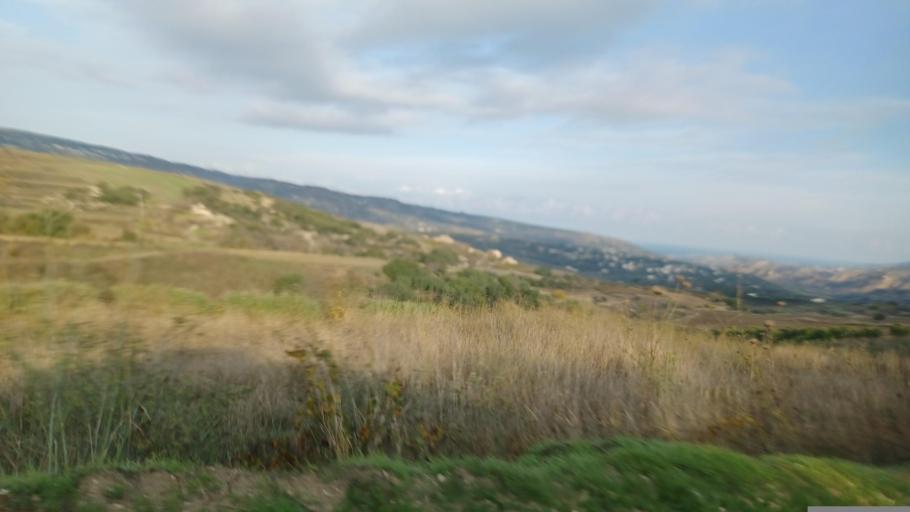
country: CY
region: Pafos
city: Tala
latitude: 34.8986
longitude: 32.4869
